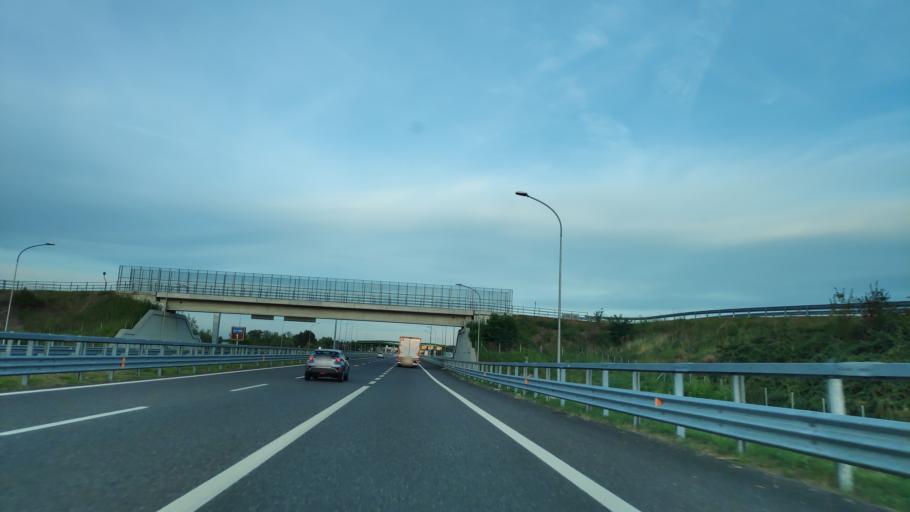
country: IT
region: Lombardy
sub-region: Citta metropolitana di Milano
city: Liscate
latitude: 45.4662
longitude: 9.4194
